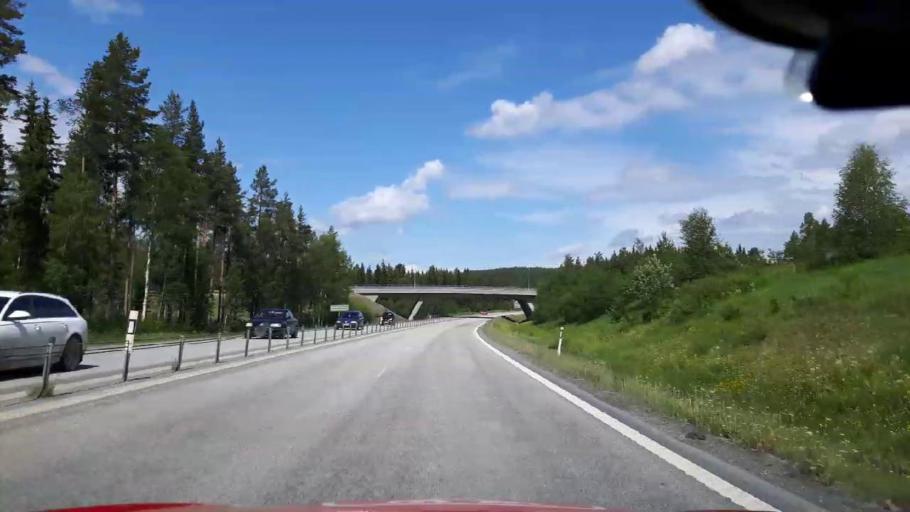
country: SE
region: Jaemtland
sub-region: OEstersunds Kommun
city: Ostersund
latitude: 63.1846
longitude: 14.6886
